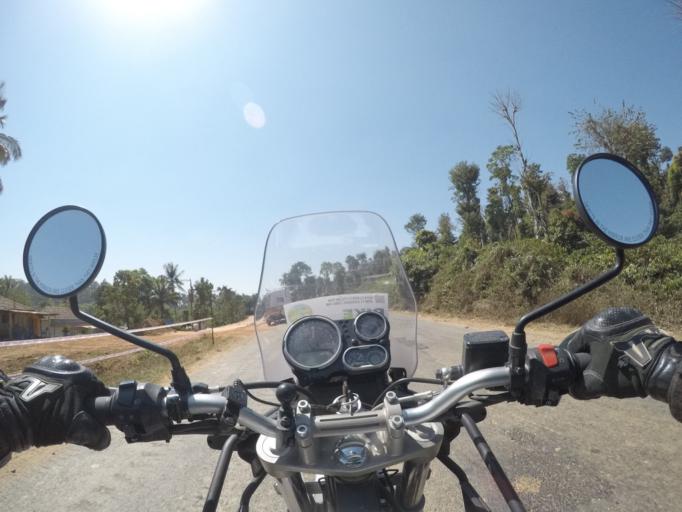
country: IN
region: Karnataka
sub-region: Hassan
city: Sakleshpur
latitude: 12.9574
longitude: 75.8380
